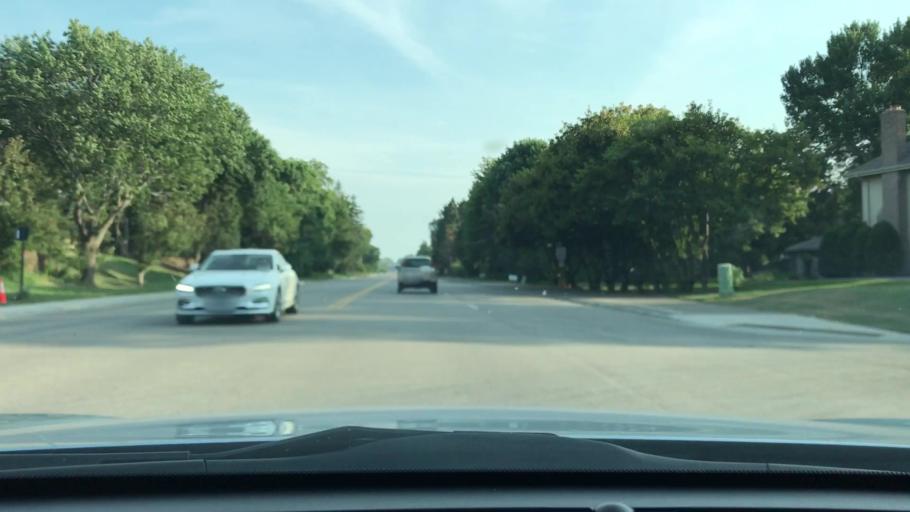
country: US
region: Minnesota
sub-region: Hennepin County
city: Plymouth
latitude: 45.0384
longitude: -93.4818
